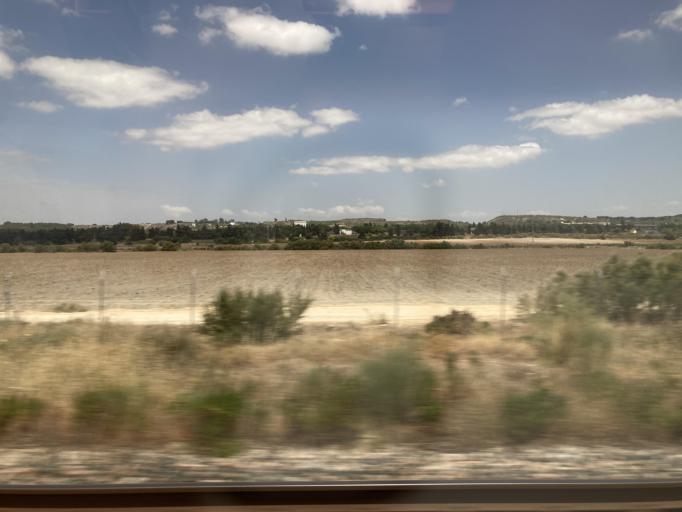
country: ES
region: Andalusia
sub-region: Provincia de Cadiz
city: El Puerto de Santa Maria
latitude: 36.6171
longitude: -6.1907
